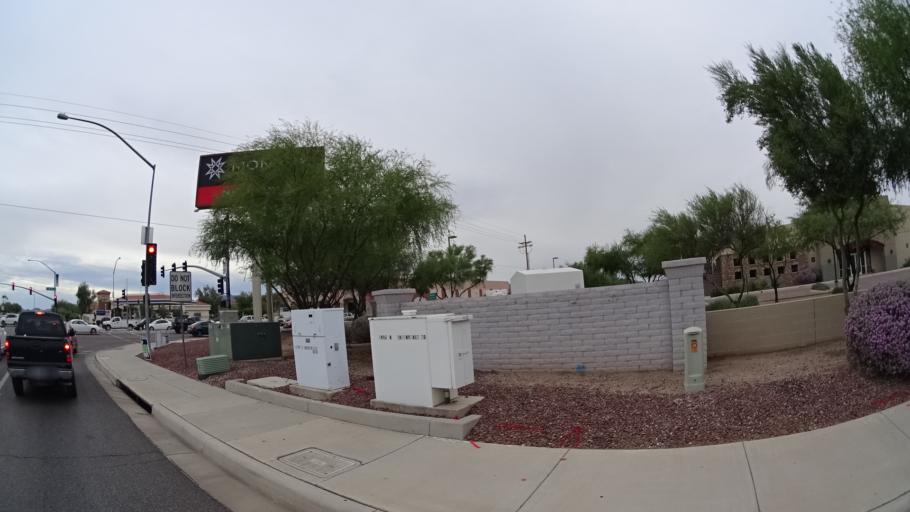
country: US
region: Arizona
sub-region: Pima County
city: Flowing Wells
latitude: 32.3238
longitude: -111.0462
